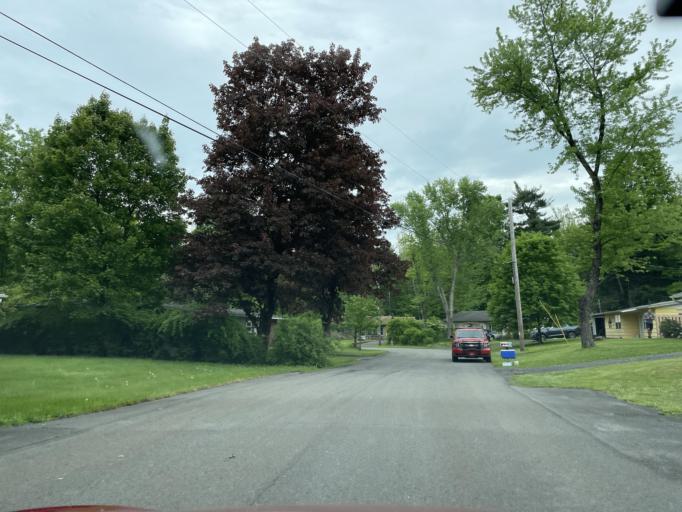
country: US
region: New York
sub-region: Ulster County
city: Woodstock
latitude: 42.0371
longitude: -74.1502
